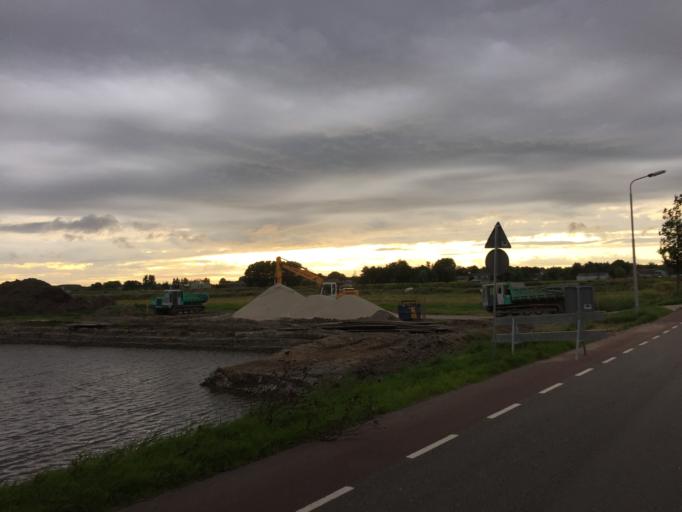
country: NL
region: South Holland
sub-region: Gemeente Pijnacker-Nootdorp
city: Pijnacker
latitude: 52.0308
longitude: 4.4561
